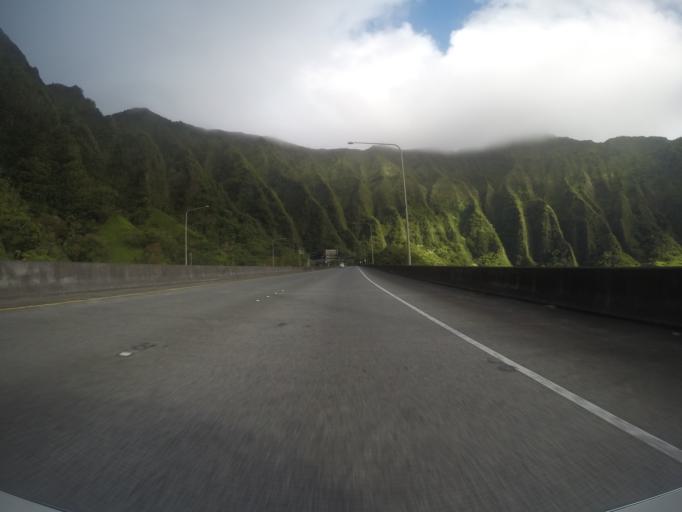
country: US
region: Hawaii
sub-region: Honolulu County
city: Kane'ohe
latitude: 21.4025
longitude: -157.8303
